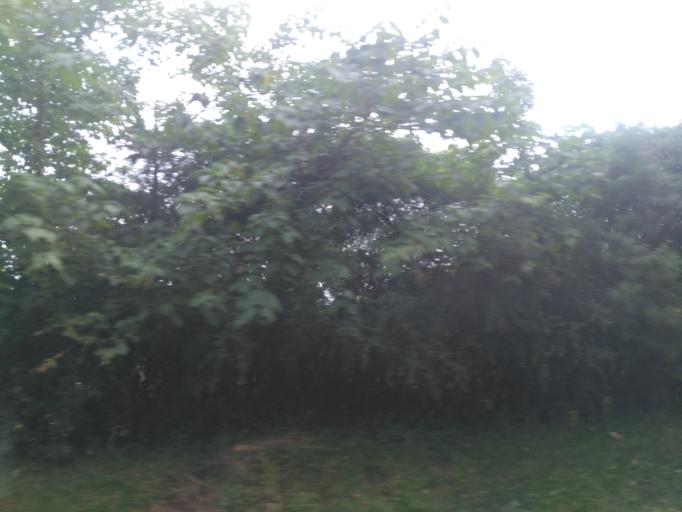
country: UG
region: Eastern Region
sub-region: Jinja District
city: Jinja
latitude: 0.4174
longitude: 33.2014
